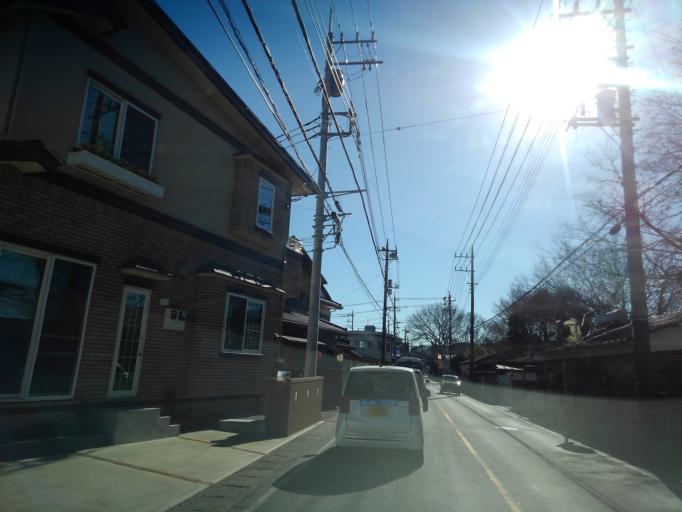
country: JP
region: Saitama
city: Hanno
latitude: 35.8437
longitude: 139.3217
